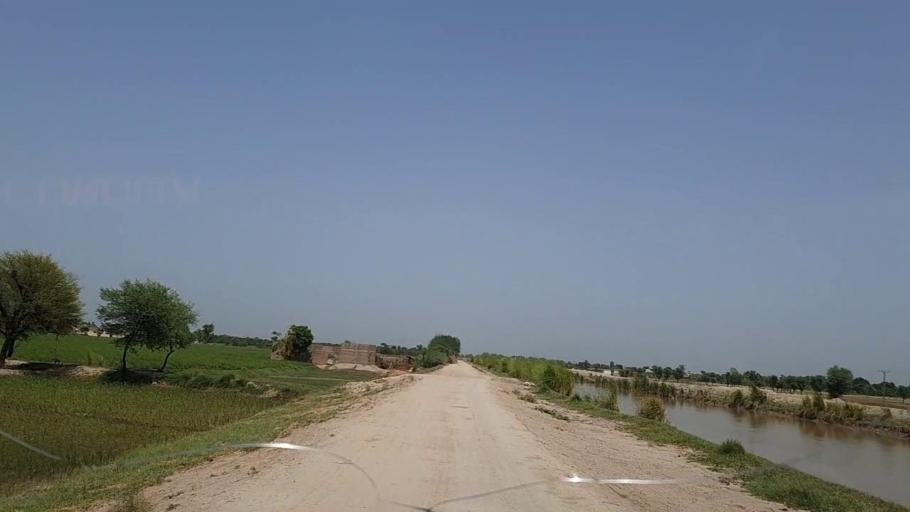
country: PK
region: Sindh
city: Tharu Shah
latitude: 26.9885
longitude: 68.0883
